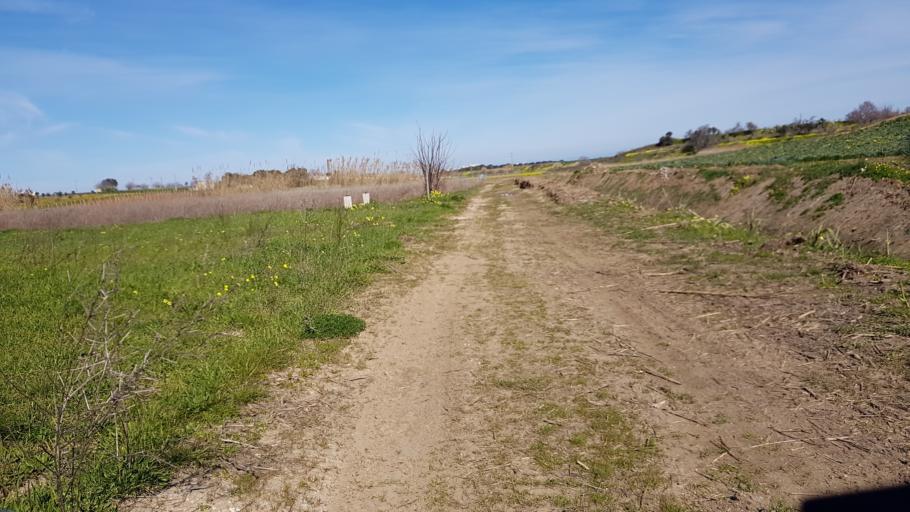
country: IT
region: Apulia
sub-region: Provincia di Brindisi
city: La Rosa
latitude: 40.6007
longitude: 17.9300
